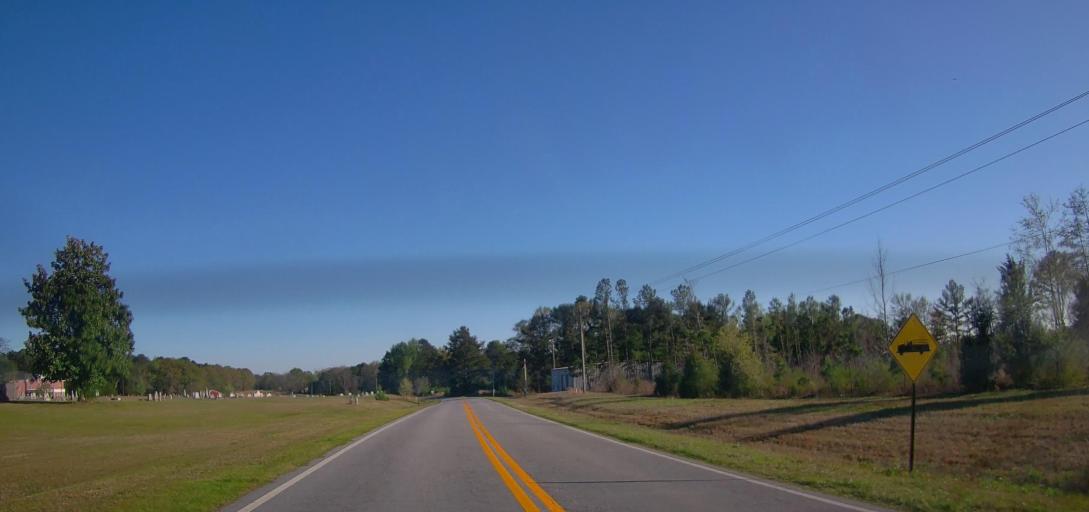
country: US
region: Georgia
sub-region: Butts County
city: Jackson
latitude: 33.3316
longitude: -83.9076
